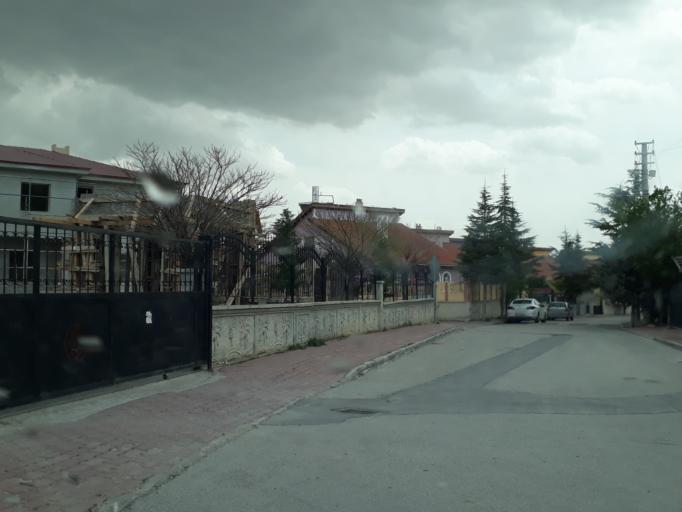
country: TR
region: Konya
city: Sille
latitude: 37.9194
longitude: 32.4625
